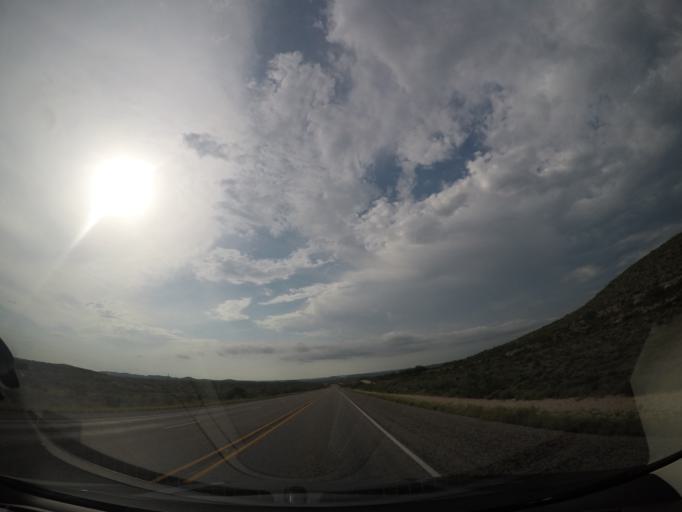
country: US
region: Texas
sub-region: Val Verde County
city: Cienegas Terrace
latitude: 29.8258
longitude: -101.6192
